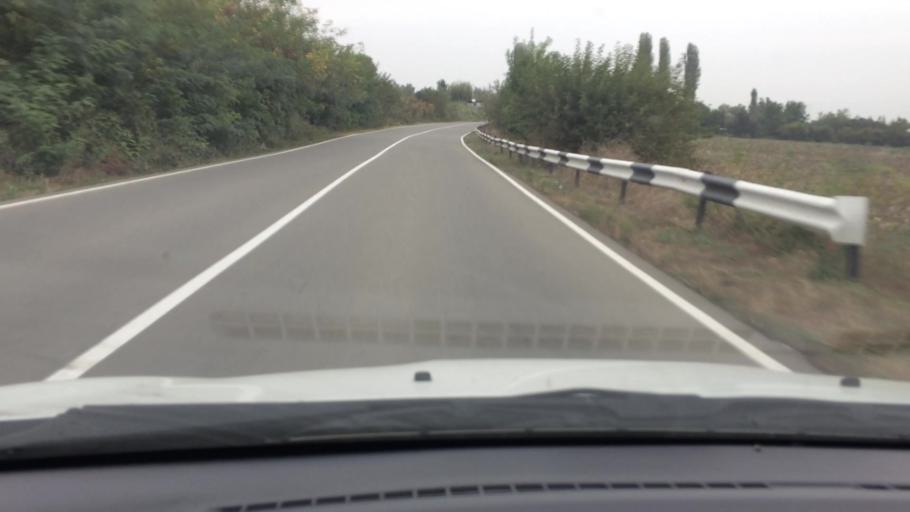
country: AM
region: Tavush
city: Bagratashen
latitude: 41.2743
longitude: 44.7905
